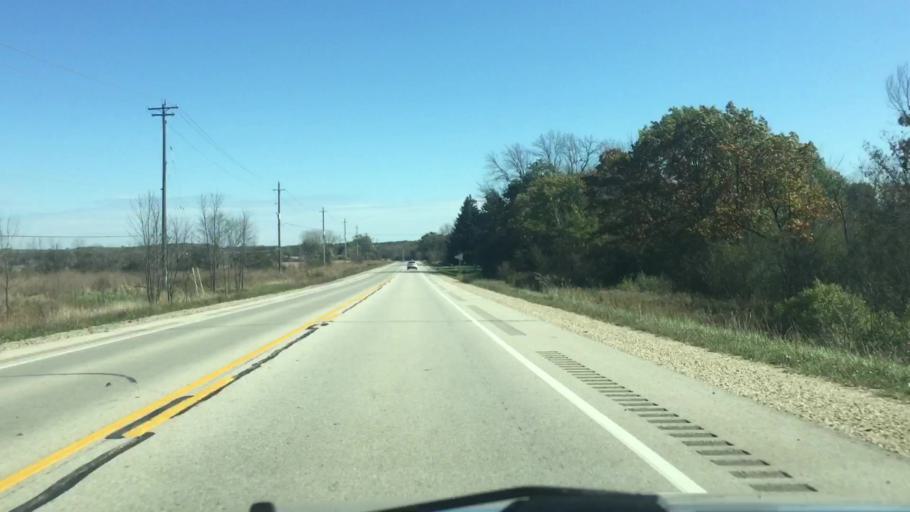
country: US
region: Wisconsin
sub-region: Waukesha County
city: Wales
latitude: 42.9591
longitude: -88.3503
